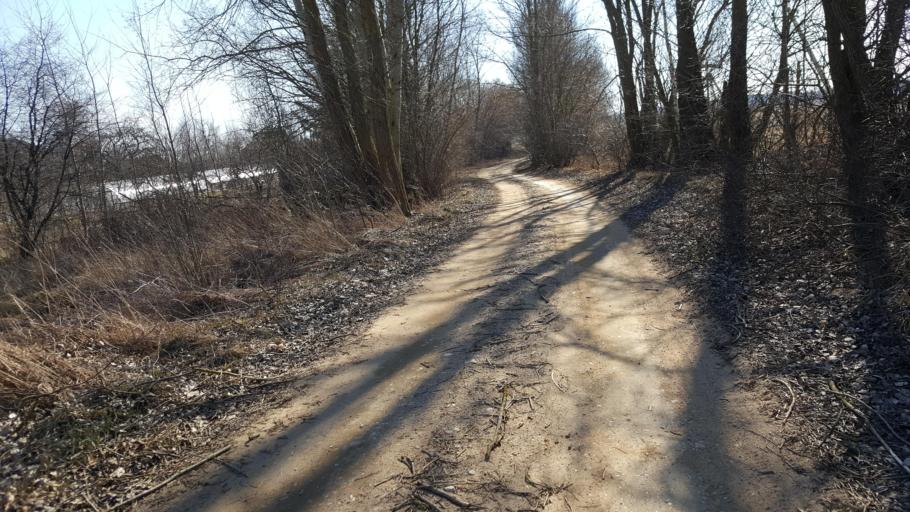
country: BY
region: Brest
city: Kamyanyets
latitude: 52.3633
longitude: 23.7619
